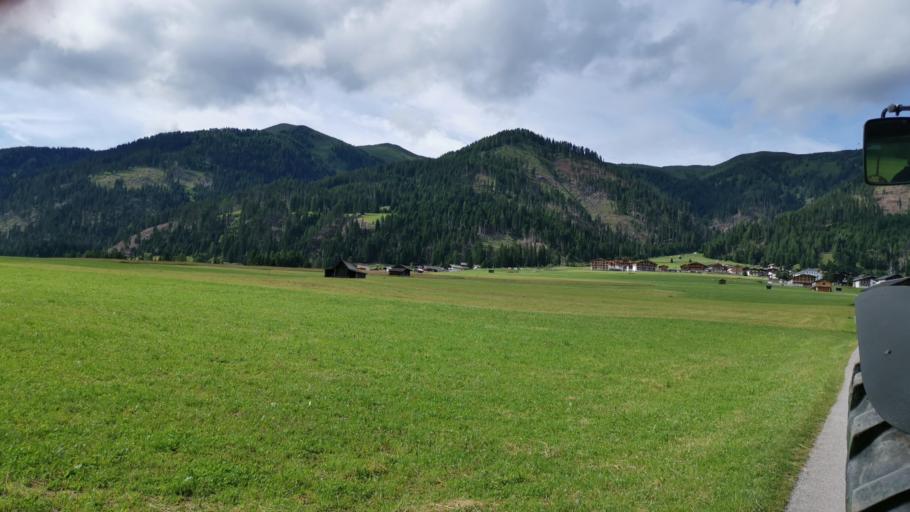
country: AT
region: Tyrol
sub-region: Politischer Bezirk Lienz
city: Obertilliach
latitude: 46.7021
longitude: 12.6090
